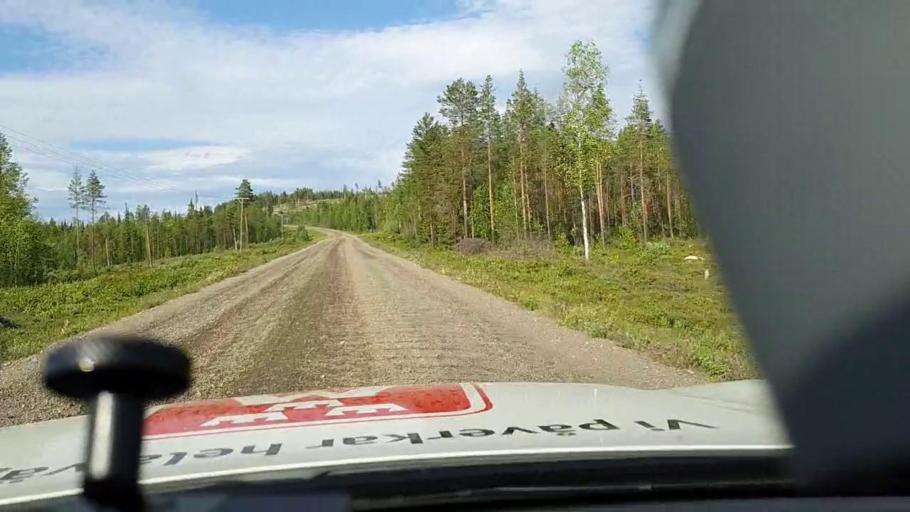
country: SE
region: Norrbotten
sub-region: Alvsbyns Kommun
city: AElvsbyn
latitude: 66.1630
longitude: 21.0520
